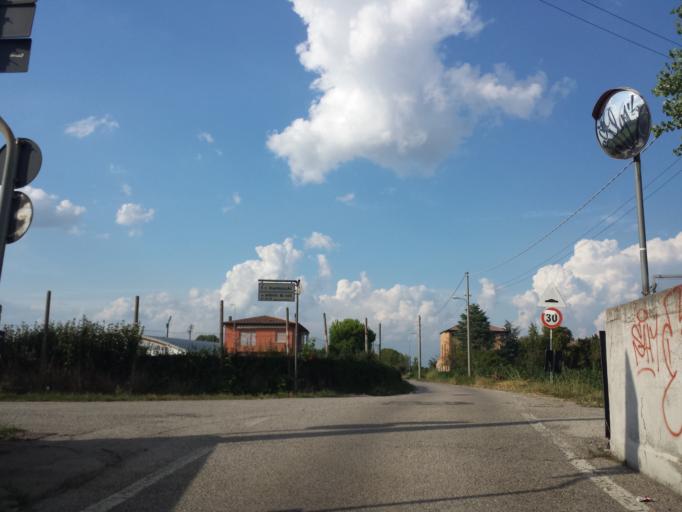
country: IT
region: Veneto
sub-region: Provincia di Padova
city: Padova
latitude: 45.4263
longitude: 11.8584
